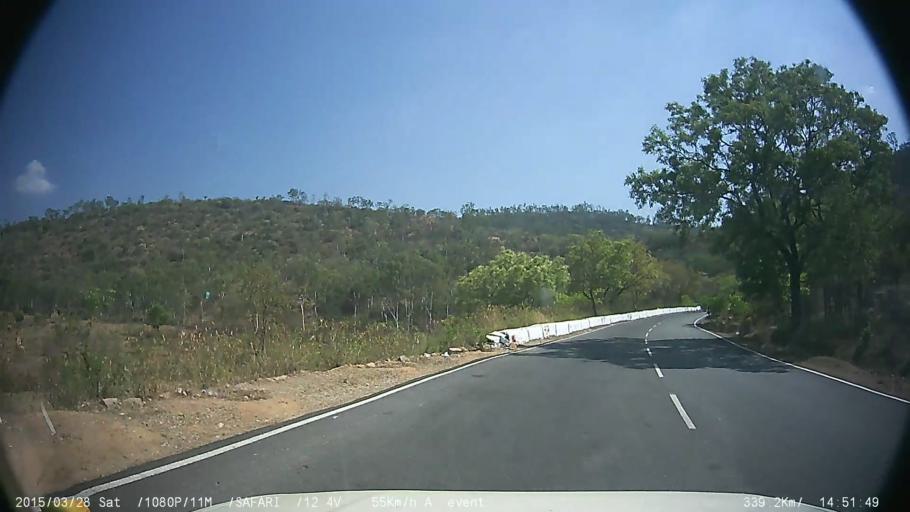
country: IN
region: Karnataka
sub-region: Mysore
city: Mysore
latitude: 12.2868
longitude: 76.6869
